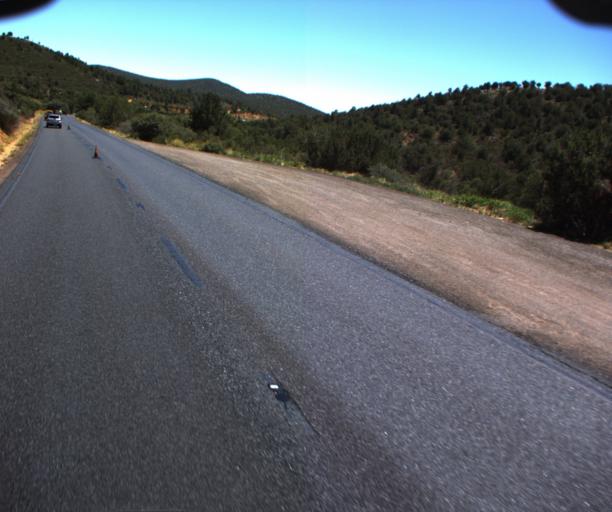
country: US
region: Arizona
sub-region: Gila County
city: Payson
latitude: 34.1988
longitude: -111.3303
